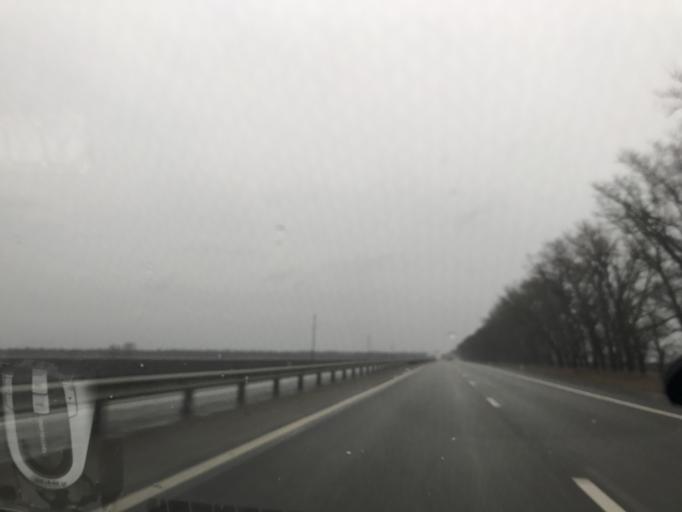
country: RU
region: Krasnodarskiy
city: Kislyakovskaya
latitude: 46.3822
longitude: 39.7448
